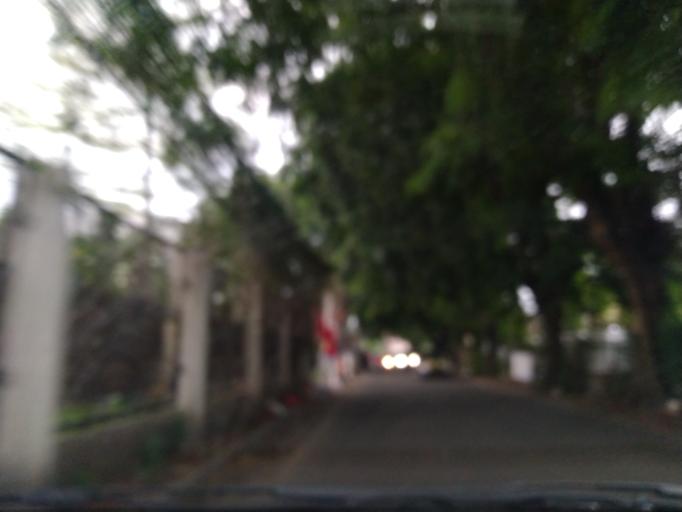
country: ID
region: Banten
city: South Tangerang
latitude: -6.2670
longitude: 106.7437
